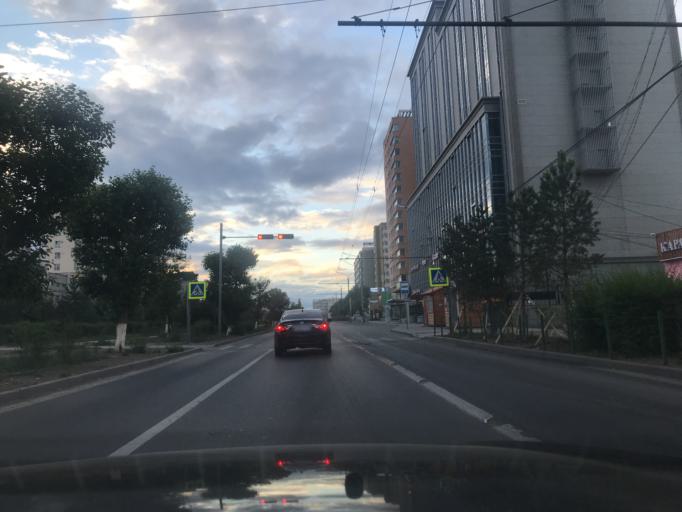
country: MN
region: Ulaanbaatar
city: Ulaanbaatar
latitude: 47.9168
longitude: 106.9596
